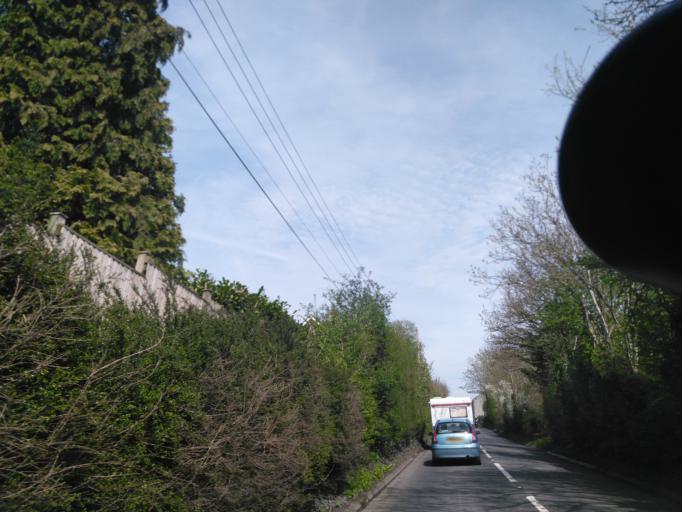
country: GB
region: England
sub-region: Somerset
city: Shepton Mallet
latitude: 51.1689
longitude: -2.5788
